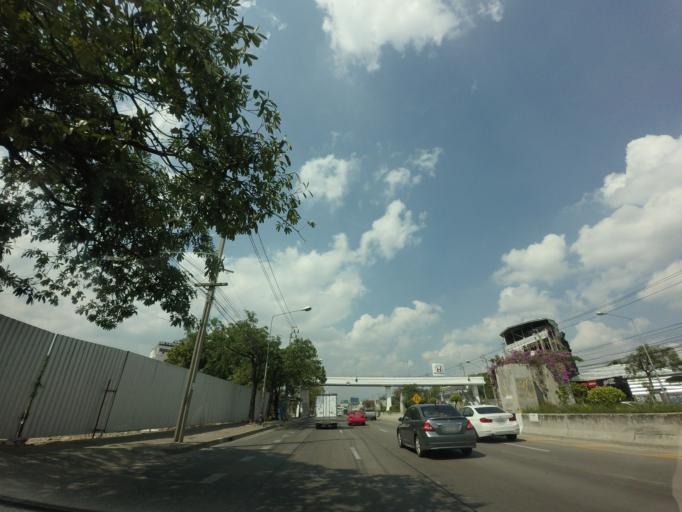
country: TH
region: Bangkok
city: Lat Phrao
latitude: 13.8382
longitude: 100.6013
